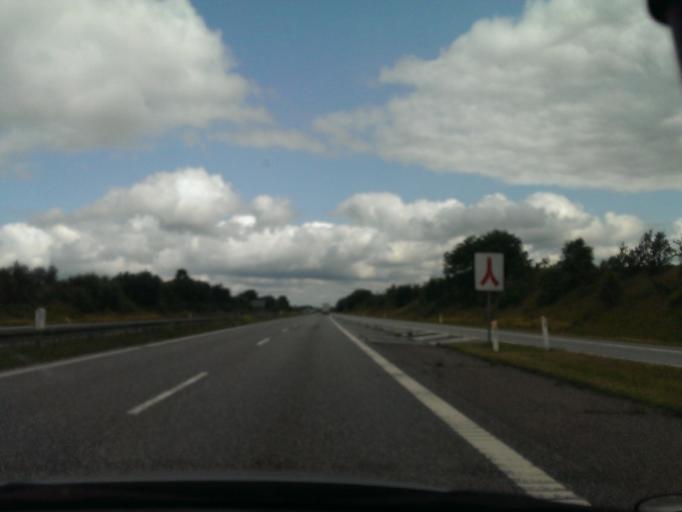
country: DK
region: North Denmark
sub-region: Mariagerfjord Kommune
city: Hobro
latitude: 56.6703
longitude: 9.7334
